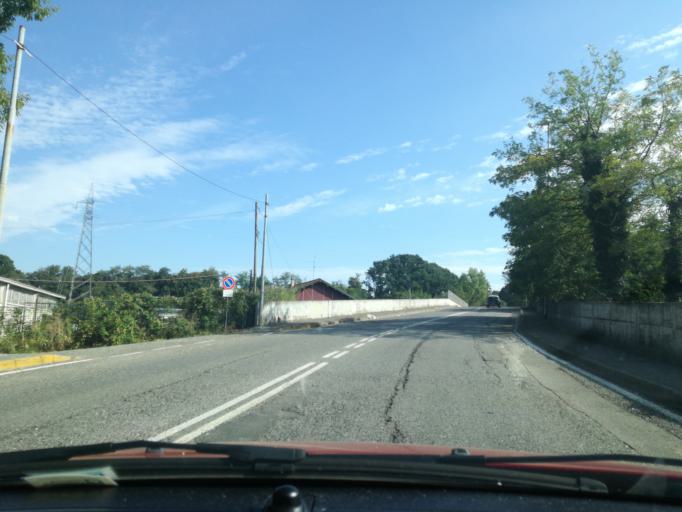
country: IT
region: Lombardy
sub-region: Provincia di Monza e Brianza
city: Carnate
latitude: 45.6564
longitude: 9.3773
